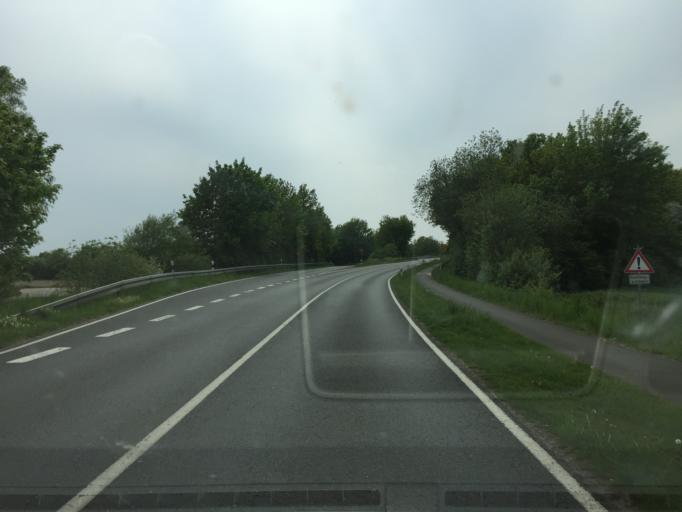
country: DE
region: Lower Saxony
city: Bassum
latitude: 52.8654
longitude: 8.7439
